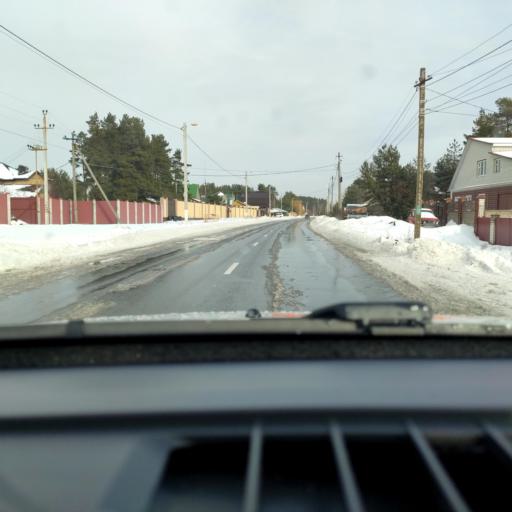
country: RU
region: Voronezj
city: Podgornoye
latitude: 51.7773
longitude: 39.1294
